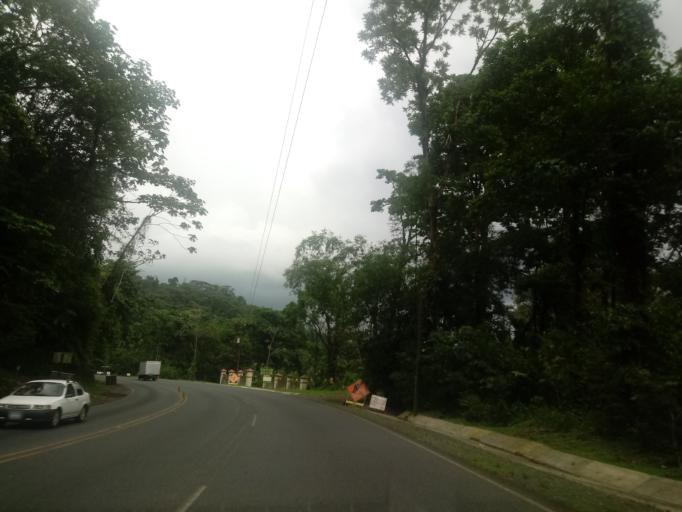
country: CR
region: San Jose
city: Dulce Nombre de Jesus
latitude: 10.1838
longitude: -83.9158
